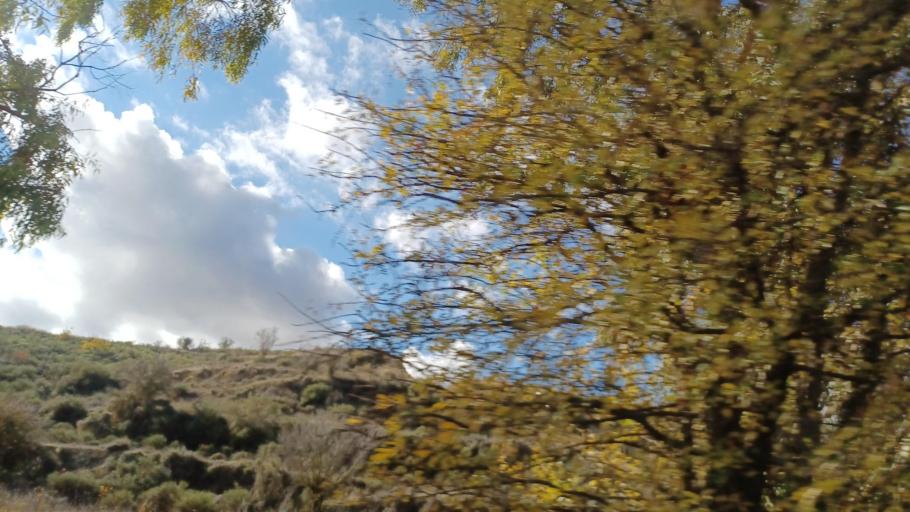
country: CY
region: Limassol
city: Pachna
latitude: 34.8004
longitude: 32.7965
